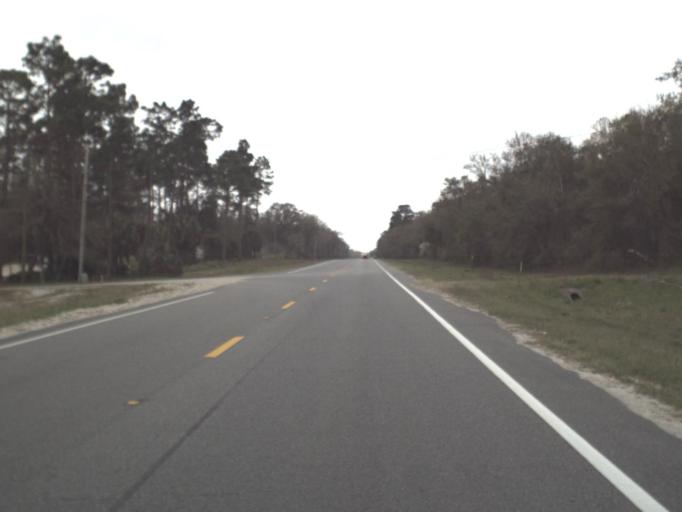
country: US
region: Florida
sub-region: Wakulla County
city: Crawfordville
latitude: 30.1223
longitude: -84.3686
